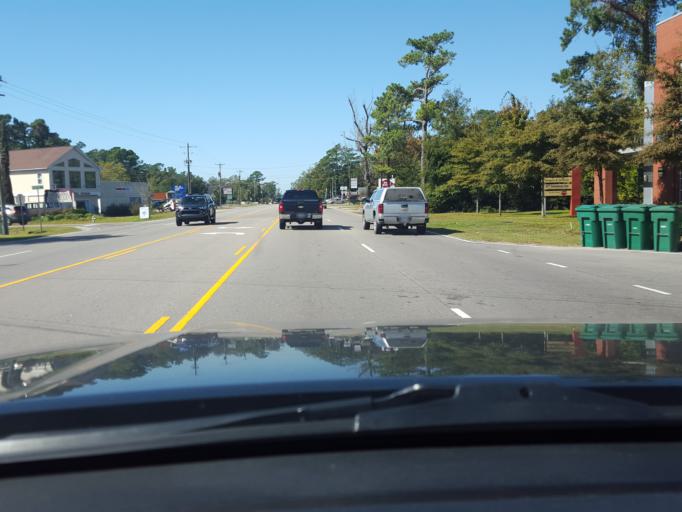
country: US
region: North Carolina
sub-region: New Hanover County
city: Seagate
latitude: 34.2096
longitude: -77.8418
